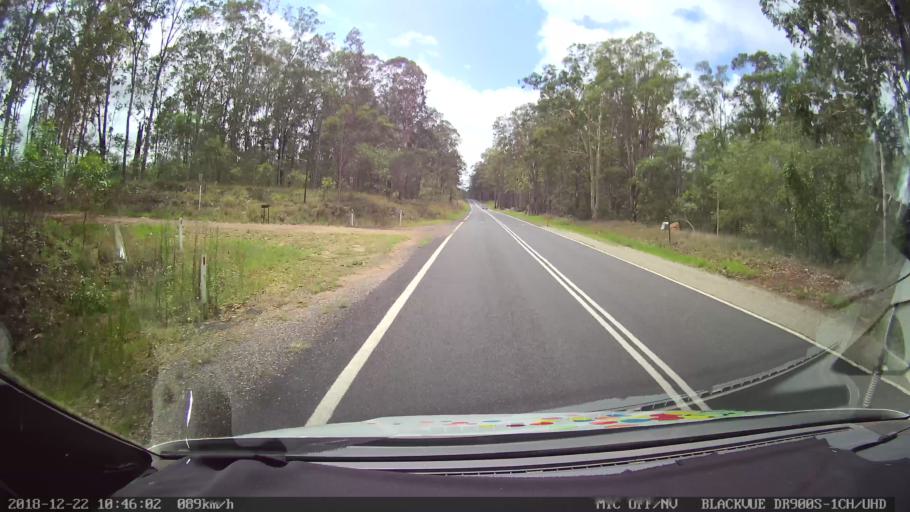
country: AU
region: New South Wales
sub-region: Clarence Valley
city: South Grafton
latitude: -29.6632
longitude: 152.8197
